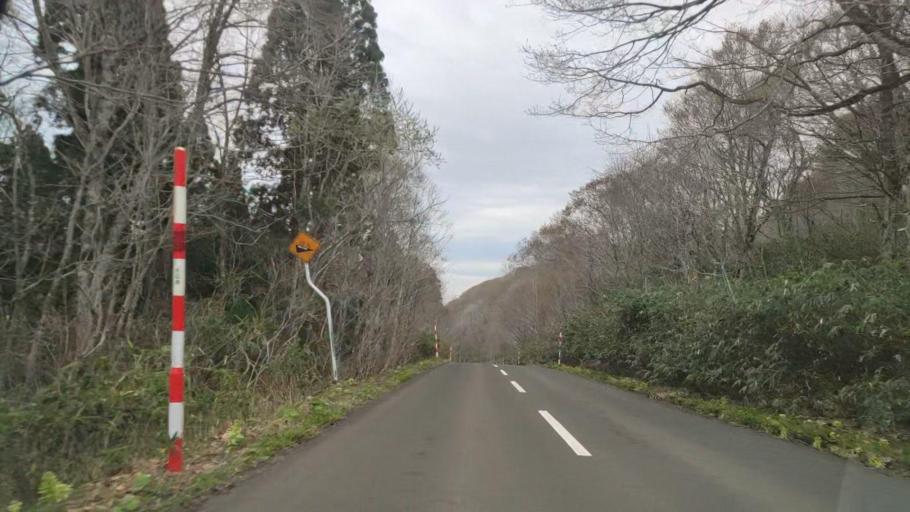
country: JP
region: Akita
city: Hanawa
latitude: 40.4147
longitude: 140.8193
